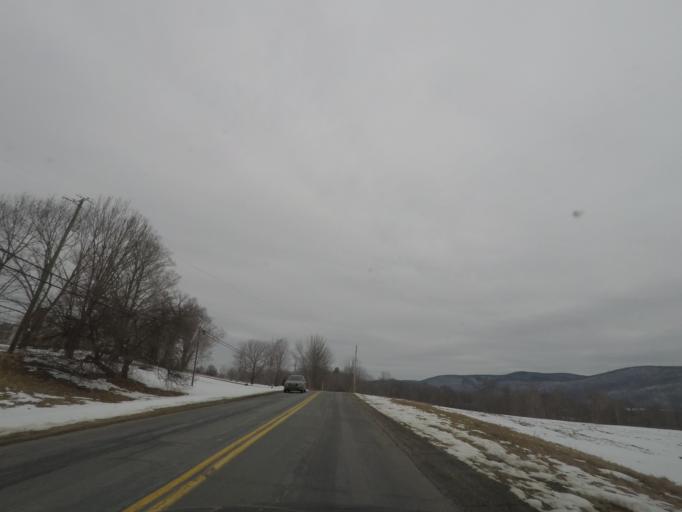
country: US
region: Massachusetts
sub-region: Berkshire County
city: Lanesborough
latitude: 42.5635
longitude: -73.3813
